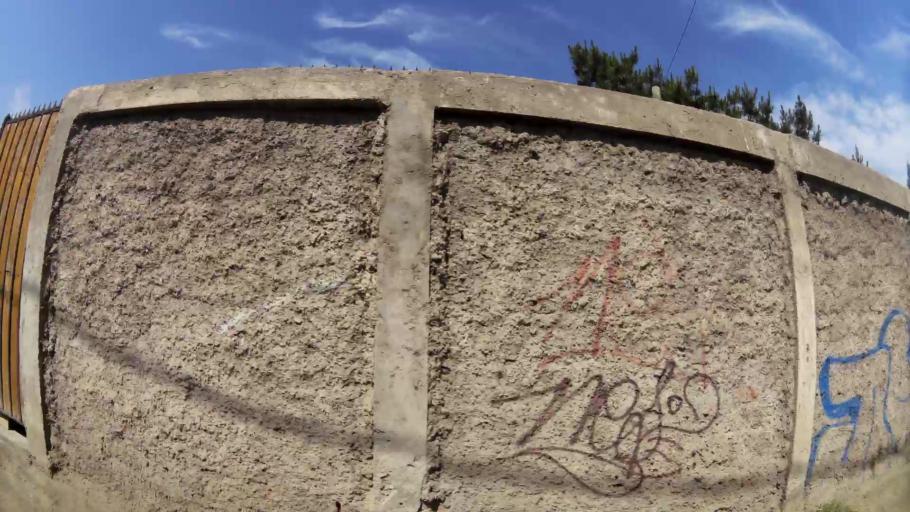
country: CL
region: Santiago Metropolitan
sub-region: Provincia de Santiago
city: La Pintana
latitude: -33.5598
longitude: -70.6376
